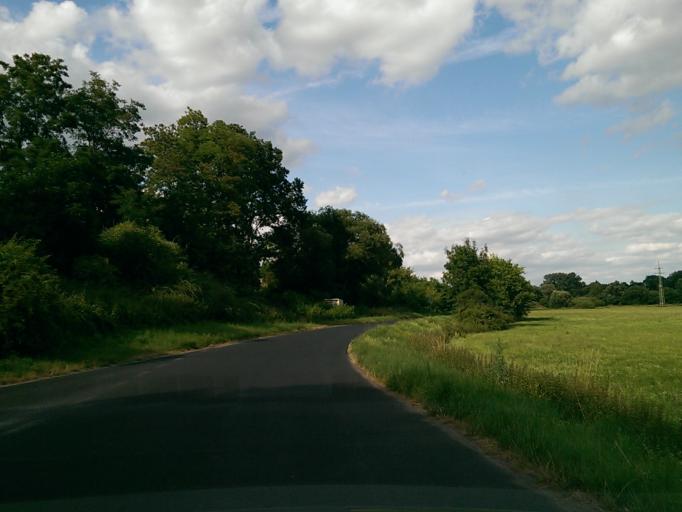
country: CZ
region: Central Bohemia
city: Bakov nad Jizerou
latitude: 50.4729
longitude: 14.9250
